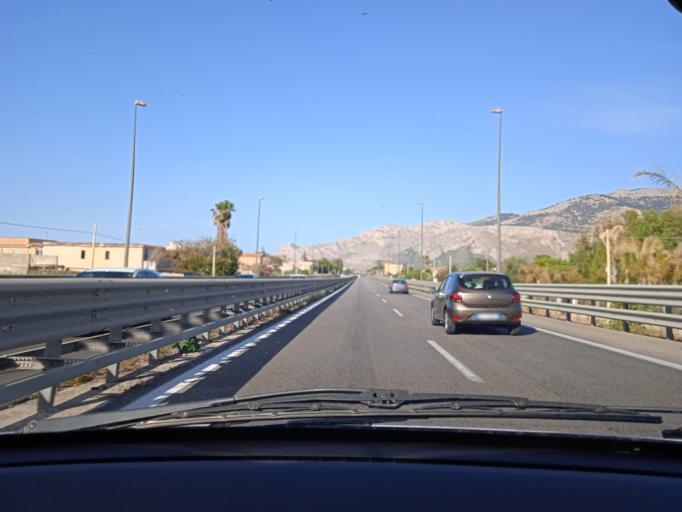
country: IT
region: Sicily
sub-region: Palermo
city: Carini
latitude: 38.1692
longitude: 13.1934
